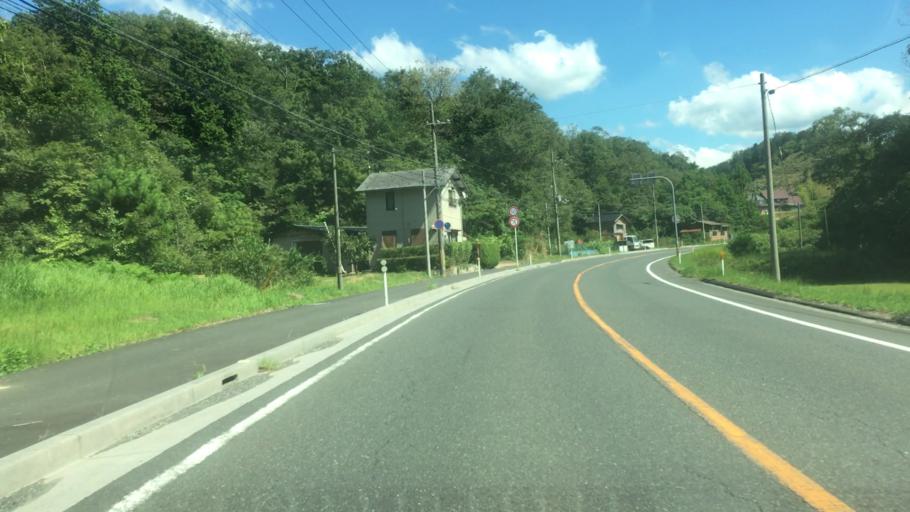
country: JP
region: Hyogo
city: Toyooka
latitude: 35.5863
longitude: 134.9513
